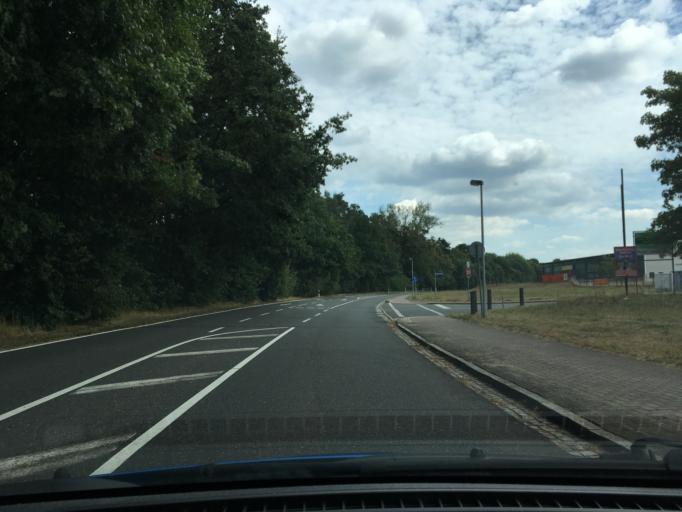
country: DE
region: Mecklenburg-Vorpommern
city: Malliss
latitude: 53.2113
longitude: 11.3134
